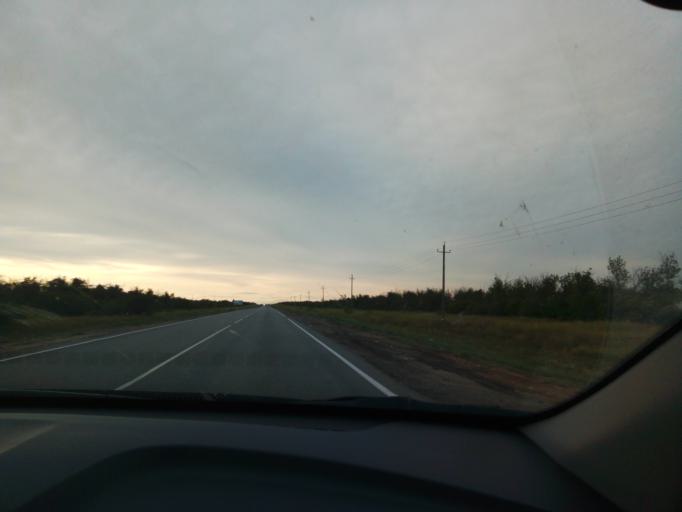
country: RU
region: Volgograd
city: Primorsk
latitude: 49.2717
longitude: 44.8763
